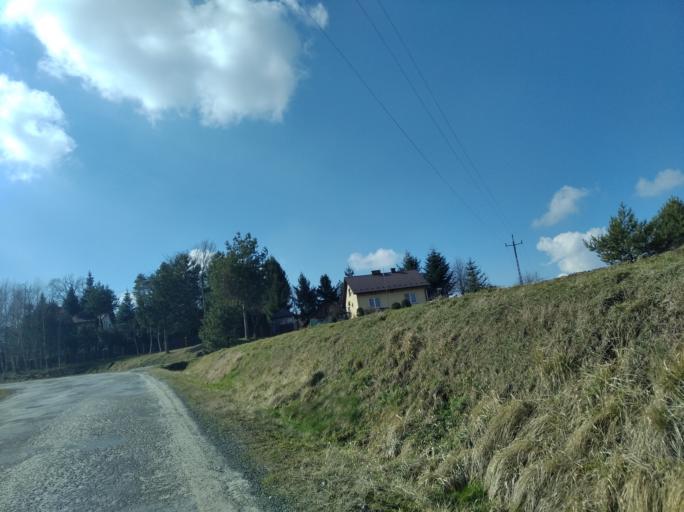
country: PL
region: Subcarpathian Voivodeship
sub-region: Powiat debicki
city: Brzostek
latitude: 49.8938
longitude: 21.4857
